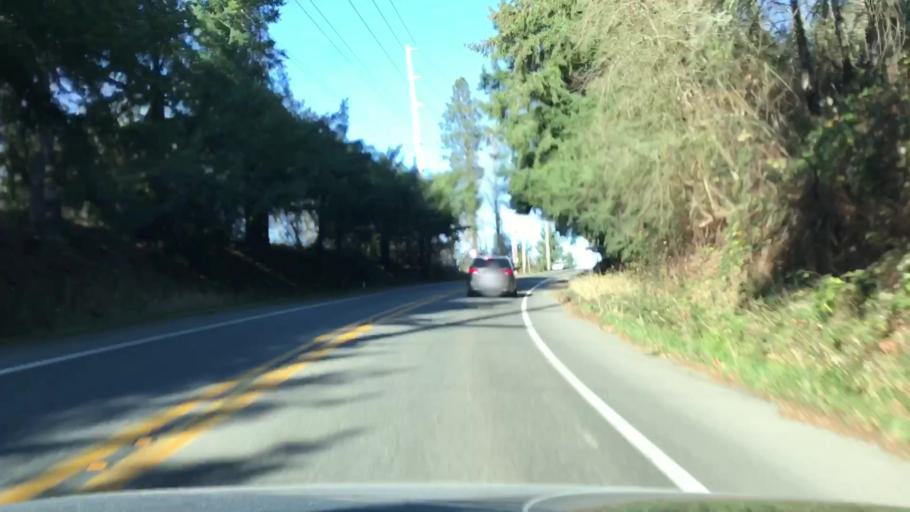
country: US
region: Washington
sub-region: King County
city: Black Diamond
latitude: 47.3058
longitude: -122.0024
